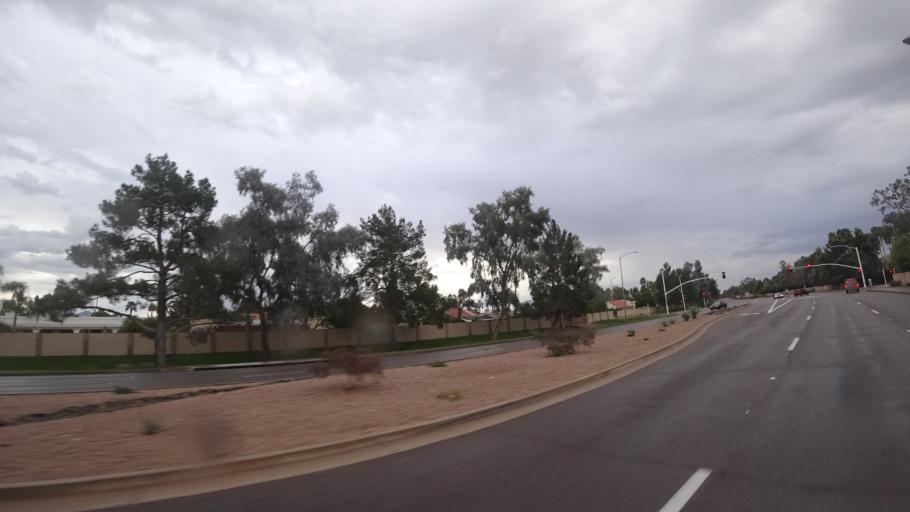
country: US
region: Arizona
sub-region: Maricopa County
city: Paradise Valley
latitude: 33.5679
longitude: -111.9032
